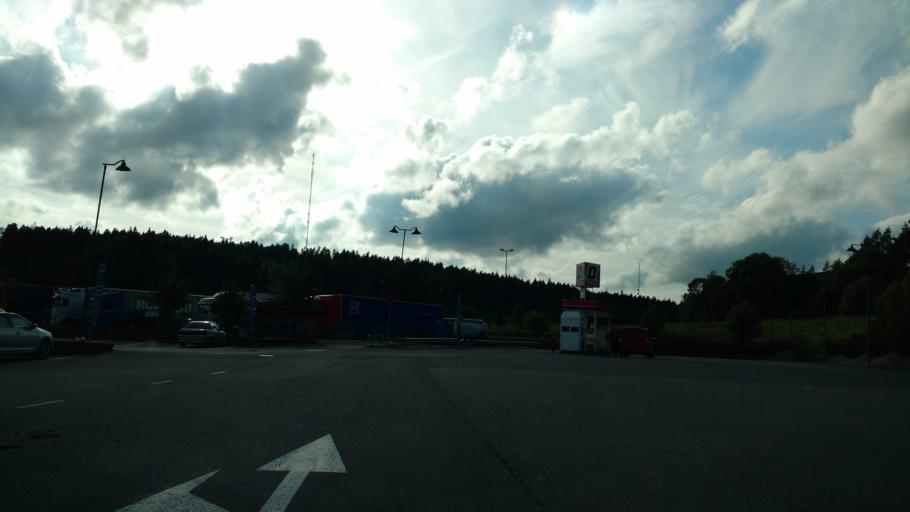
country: FI
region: Varsinais-Suomi
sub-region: Salo
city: Salo
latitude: 60.4189
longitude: 23.1636
